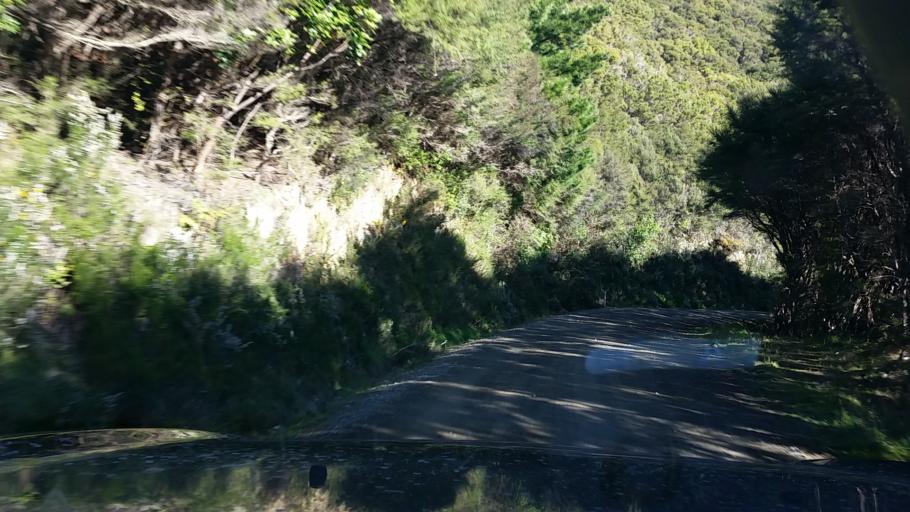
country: NZ
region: Marlborough
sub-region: Marlborough District
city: Picton
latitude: -41.1353
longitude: 174.0530
